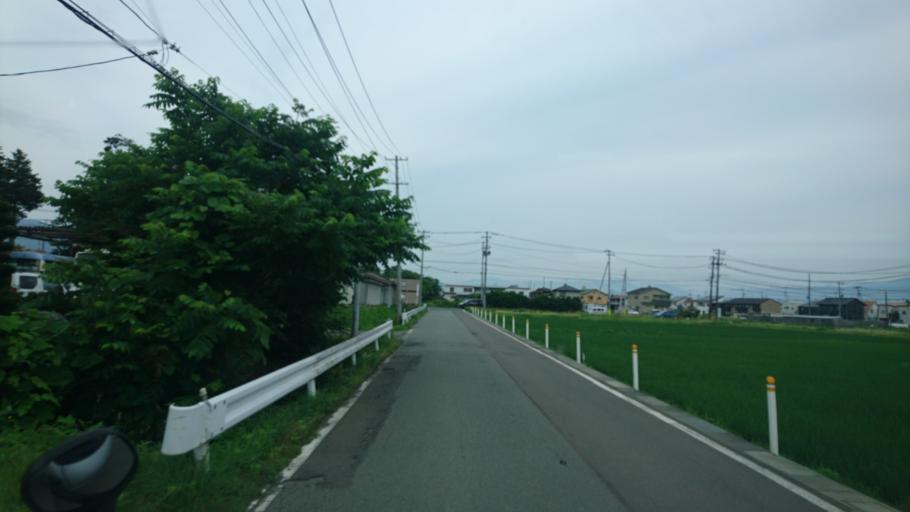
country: JP
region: Iwate
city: Morioka-shi
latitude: 39.6680
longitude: 141.1433
